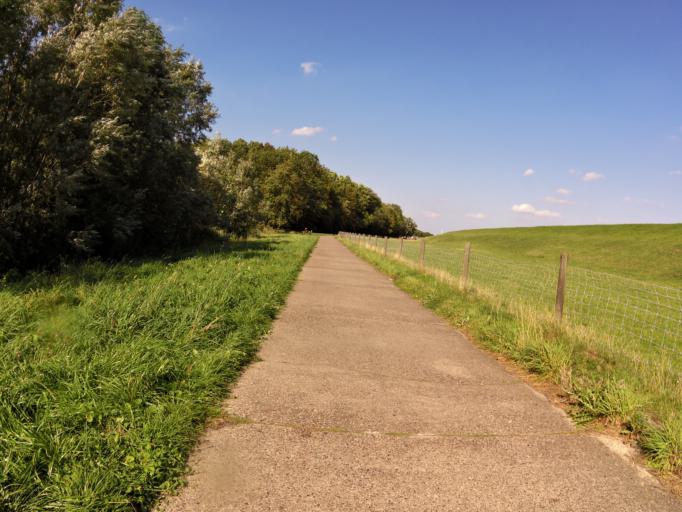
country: DE
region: Lower Saxony
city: Brake (Unterweser)
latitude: 53.4010
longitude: 8.4632
